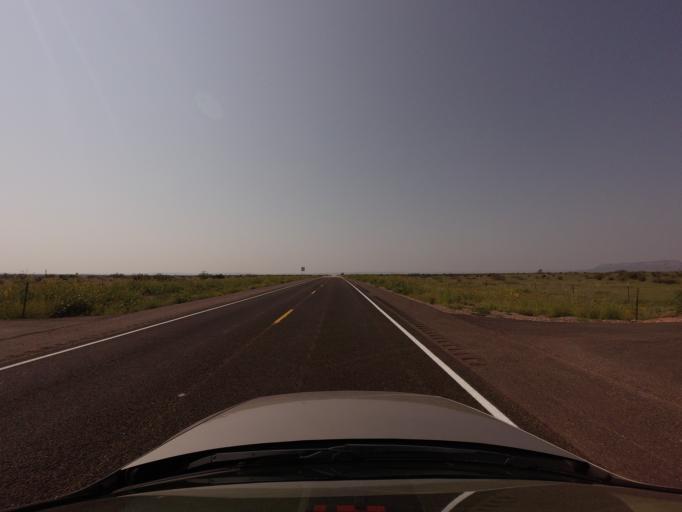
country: US
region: New Mexico
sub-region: Quay County
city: Tucumcari
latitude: 34.9734
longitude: -103.7524
